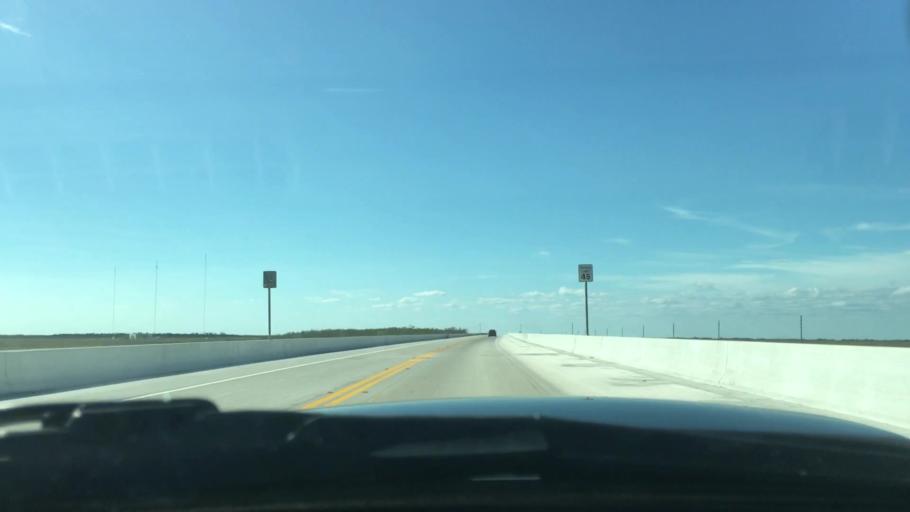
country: US
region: Florida
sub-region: Miami-Dade County
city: Kendall West
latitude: 25.7606
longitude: -80.6312
